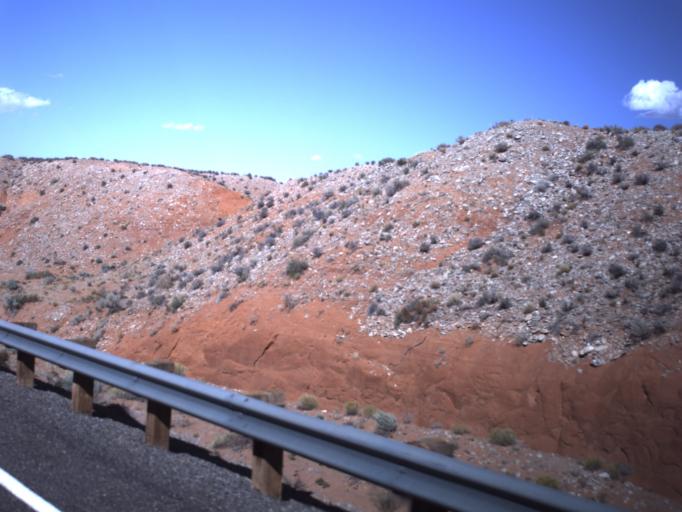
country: US
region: Utah
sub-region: Wayne County
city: Loa
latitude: 38.1370
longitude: -110.6096
